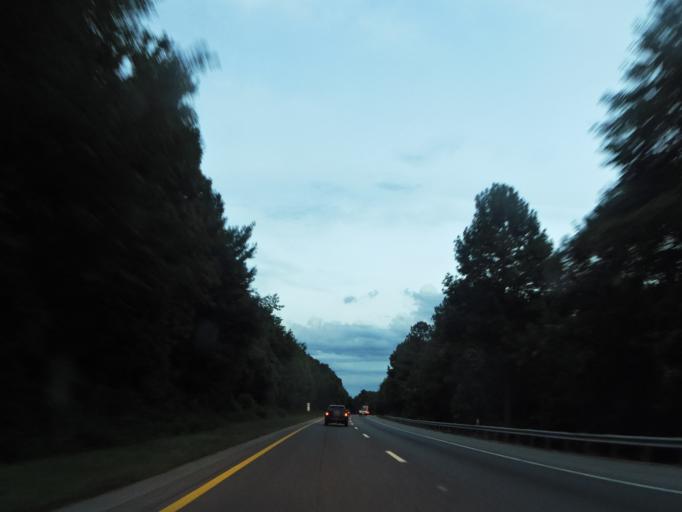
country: US
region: Tennessee
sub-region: Roane County
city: Rockwood
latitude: 35.8955
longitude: -84.6596
